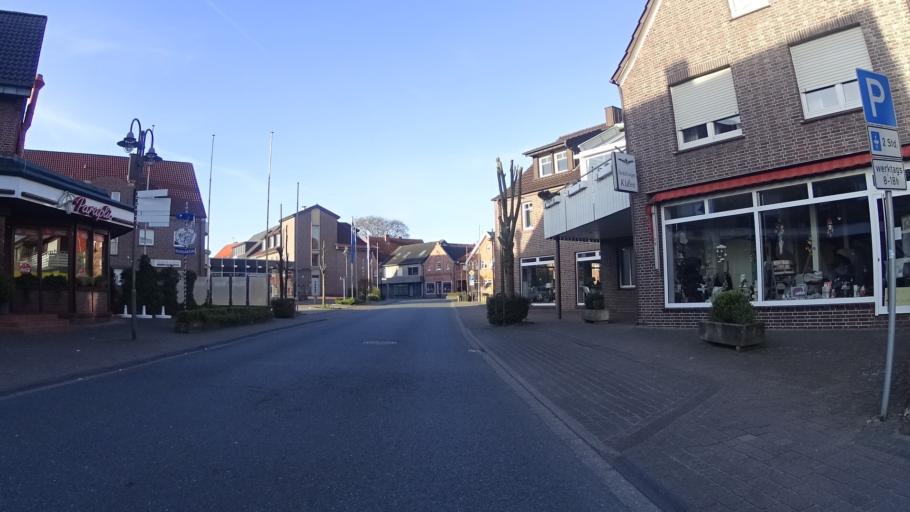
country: DE
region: Lower Saxony
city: Lathen
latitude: 52.8629
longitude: 7.3149
